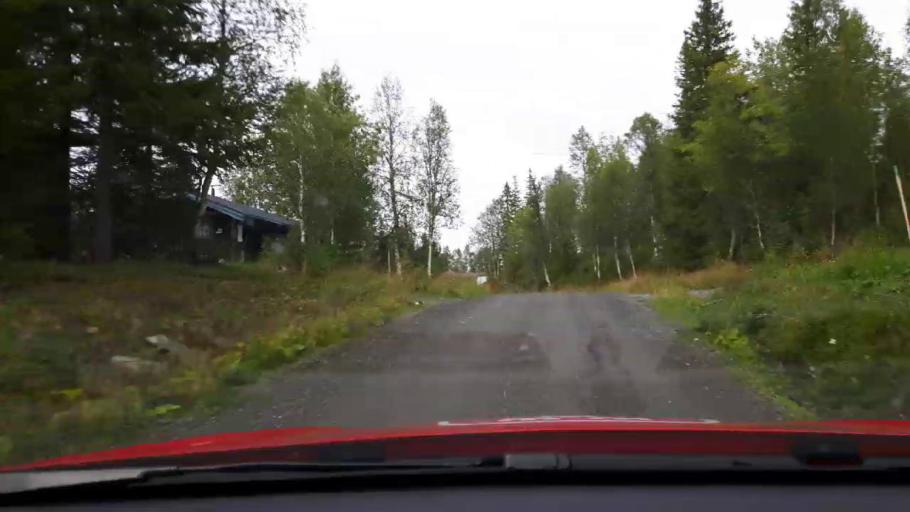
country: SE
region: Jaemtland
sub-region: Are Kommun
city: Are
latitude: 63.7749
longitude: 13.0702
